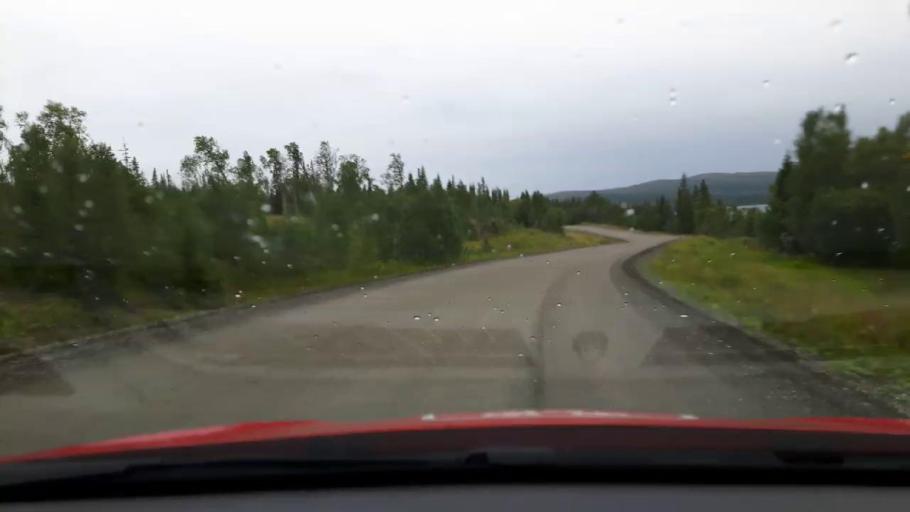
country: NO
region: Nord-Trondelag
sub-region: Meraker
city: Meraker
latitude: 63.5584
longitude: 12.3705
